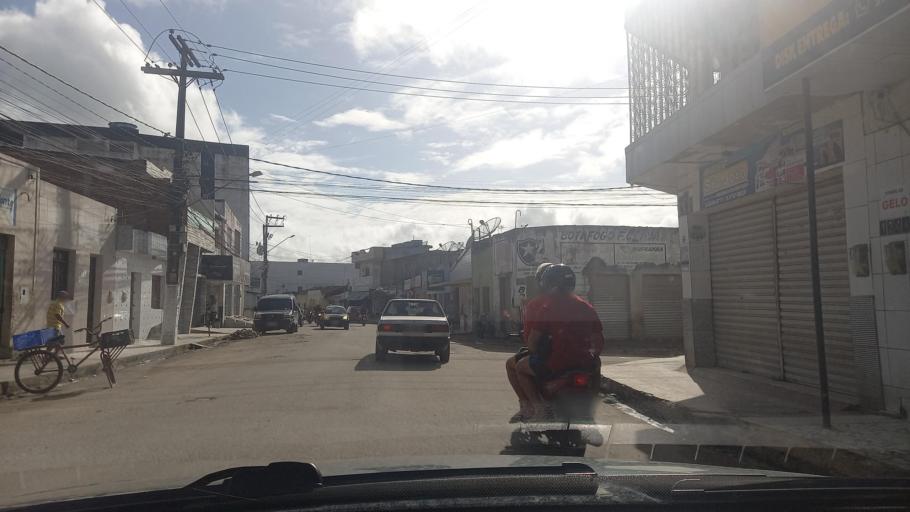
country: BR
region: Pernambuco
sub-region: Vitoria De Santo Antao
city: Vitoria de Santo Antao
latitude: -8.1067
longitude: -35.2839
